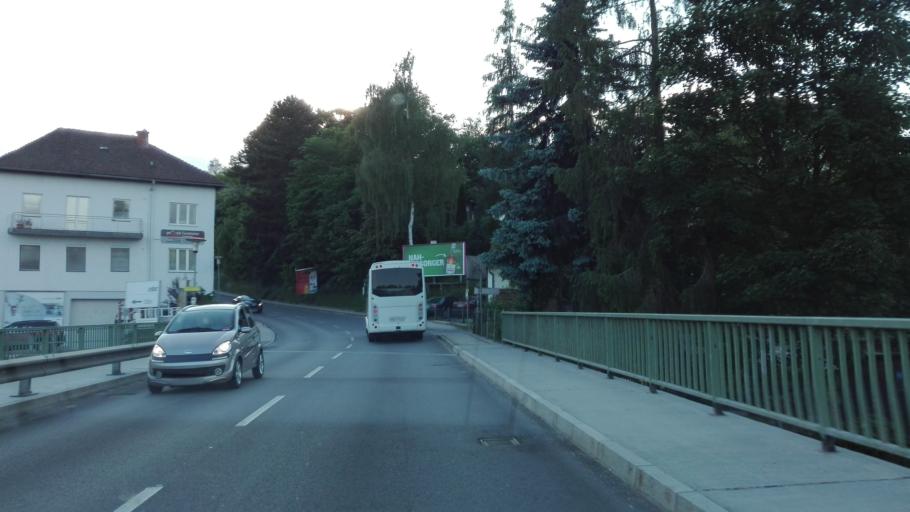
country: AT
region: Upper Austria
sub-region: Politischer Bezirk Urfahr-Umgebung
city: Engerwitzdorf
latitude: 48.3551
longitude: 14.5253
